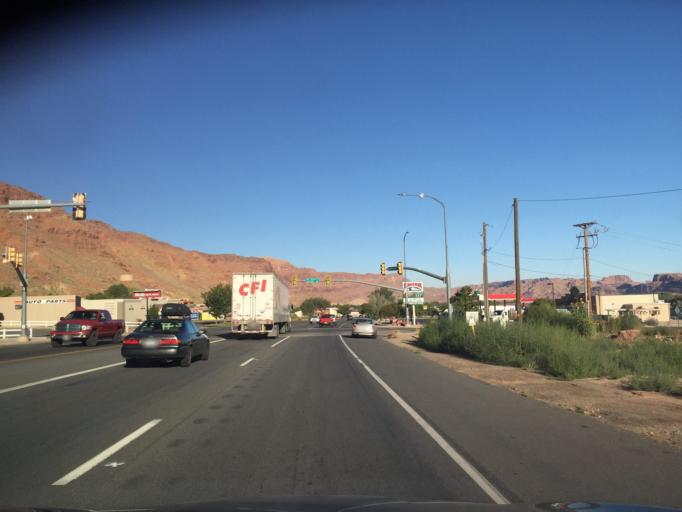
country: US
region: Utah
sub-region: Grand County
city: Moab
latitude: 38.5574
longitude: -109.5425
